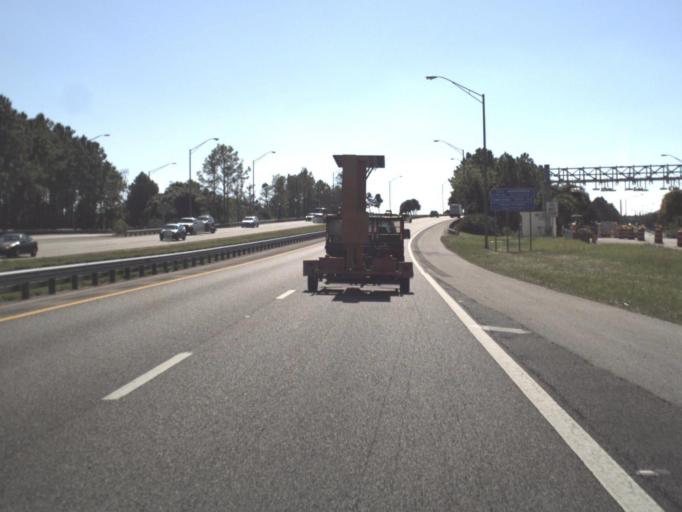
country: US
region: Florida
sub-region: Hillsborough County
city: Greater Northdale
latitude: 28.1013
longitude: -82.5423
